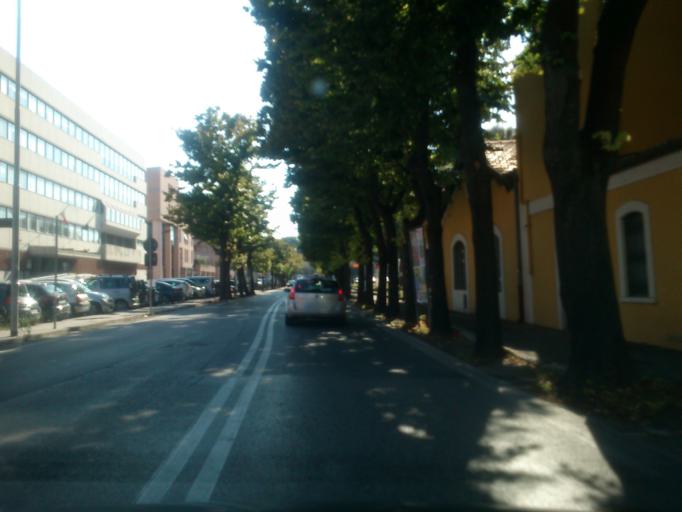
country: IT
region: The Marches
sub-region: Provincia di Pesaro e Urbino
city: Pesaro
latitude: 43.9135
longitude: 12.9075
